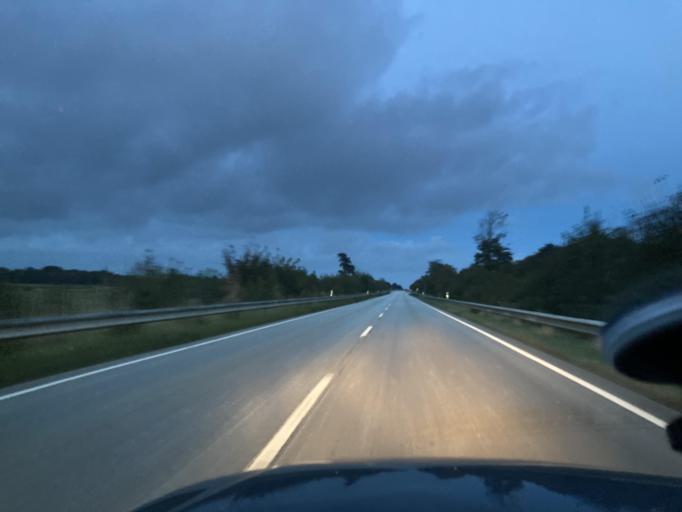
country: DE
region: Schleswig-Holstein
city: Tonning
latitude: 54.3247
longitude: 8.9404
